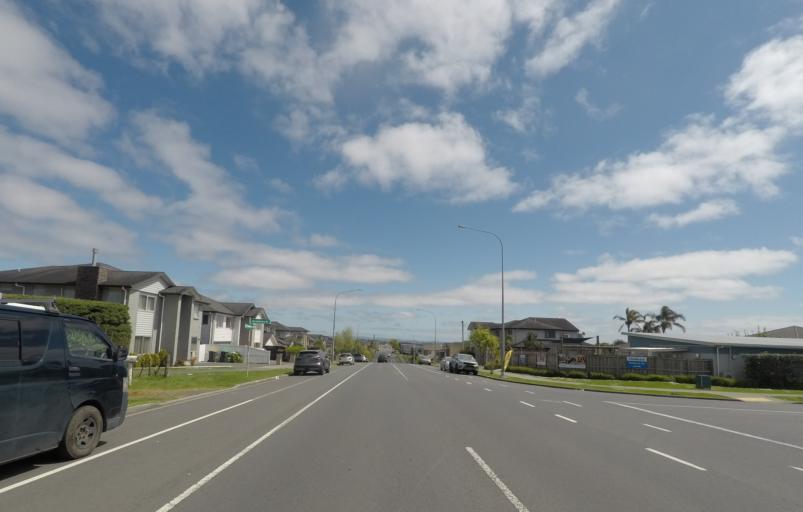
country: NZ
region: Auckland
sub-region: Auckland
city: Manukau City
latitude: -36.9743
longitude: 174.9184
